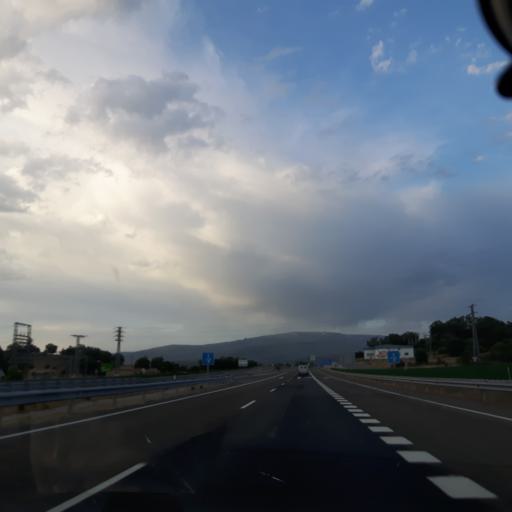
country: ES
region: Castille and Leon
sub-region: Provincia de Salamanca
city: Nava de Bejar
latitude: 40.4883
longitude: -5.6767
